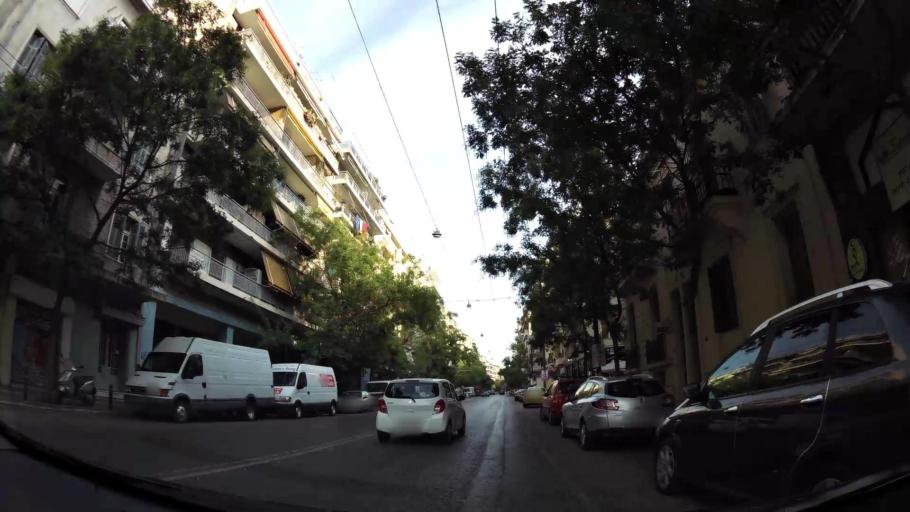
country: GR
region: Attica
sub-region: Nomarchia Athinas
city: Kipseli
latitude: 37.9980
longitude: 23.7275
